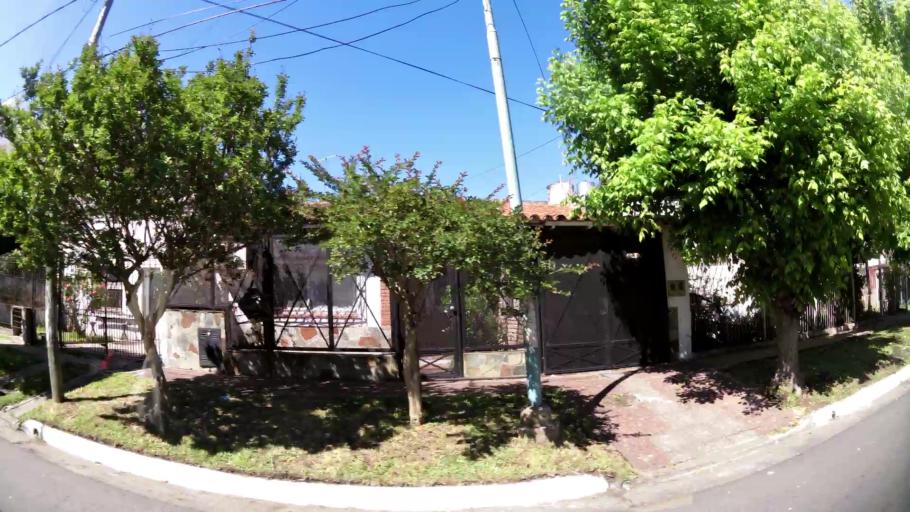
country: AR
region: Buenos Aires
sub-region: Partido de Quilmes
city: Quilmes
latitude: -34.7014
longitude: -58.2987
